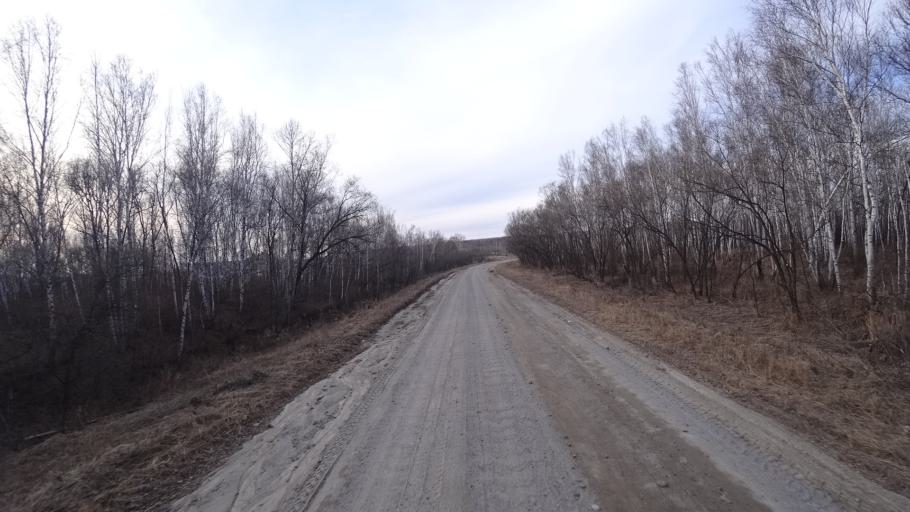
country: RU
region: Amur
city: Bureya
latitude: 50.0163
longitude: 129.7738
